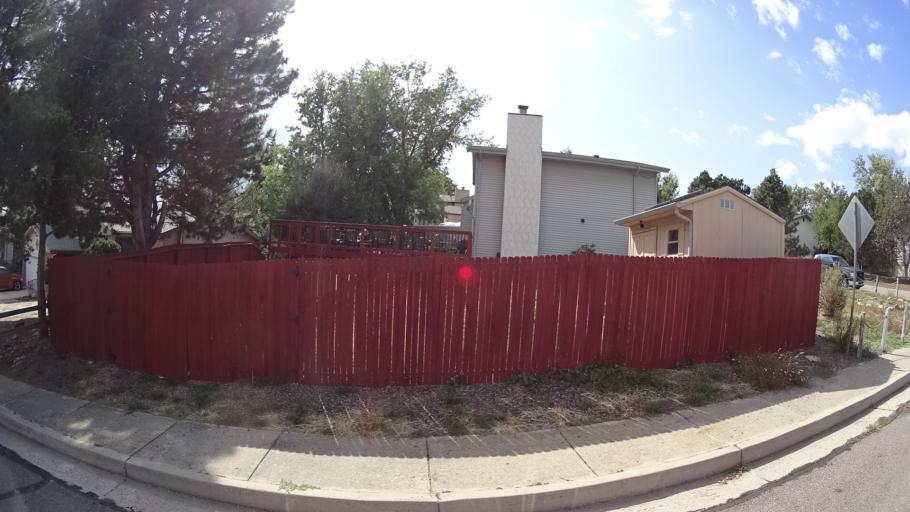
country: US
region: Colorado
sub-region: El Paso County
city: Cimarron Hills
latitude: 38.8689
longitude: -104.7328
